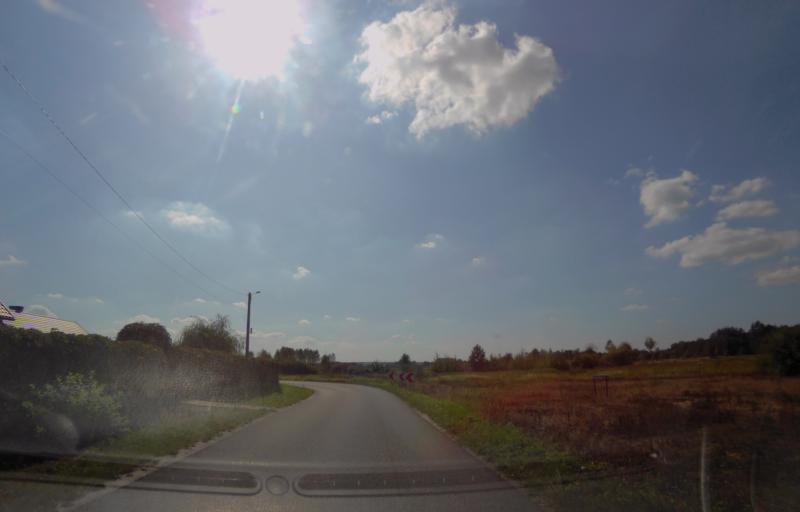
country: PL
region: Subcarpathian Voivodeship
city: Nowa Sarzyna
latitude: 50.2939
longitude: 22.3072
